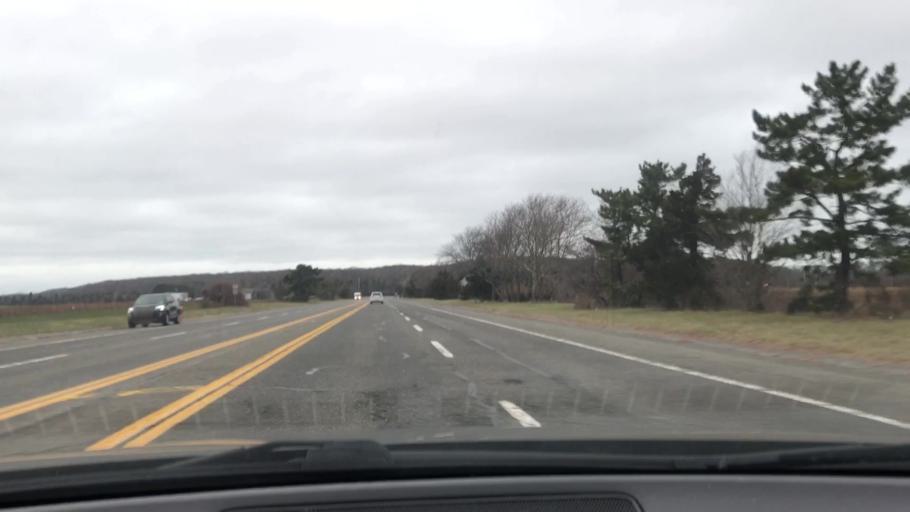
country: US
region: New York
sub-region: Suffolk County
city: Aquebogue
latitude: 40.9634
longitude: -72.6535
